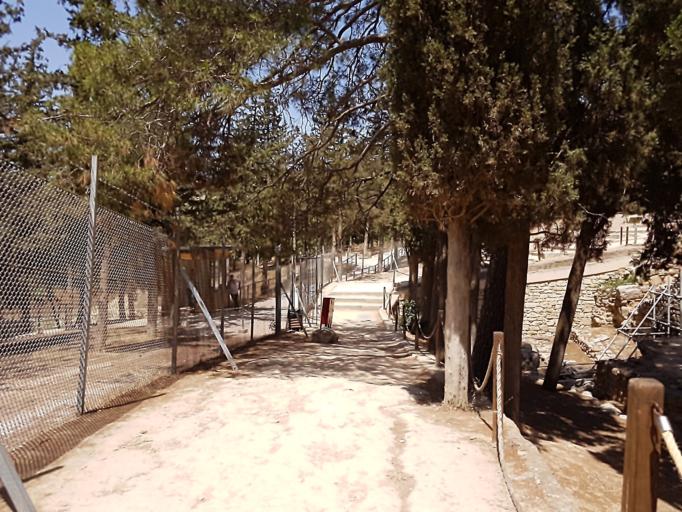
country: GR
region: Crete
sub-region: Nomos Irakleiou
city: Skalanion
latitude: 35.2973
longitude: 25.1627
